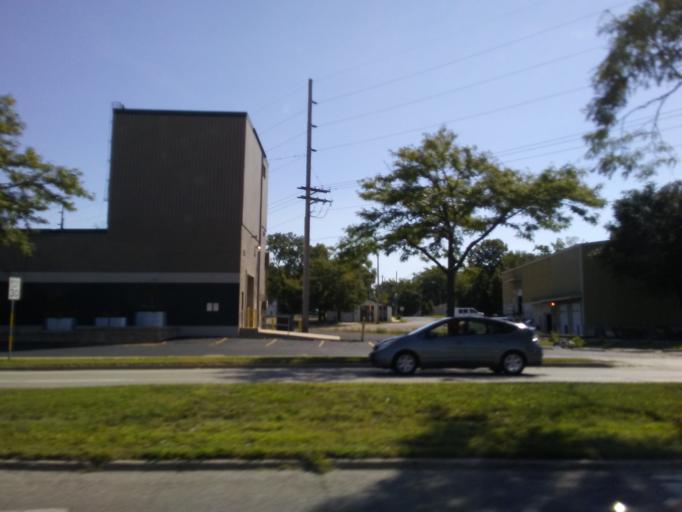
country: US
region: Wisconsin
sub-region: Dane County
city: Madison
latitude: 43.0481
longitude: -89.3941
